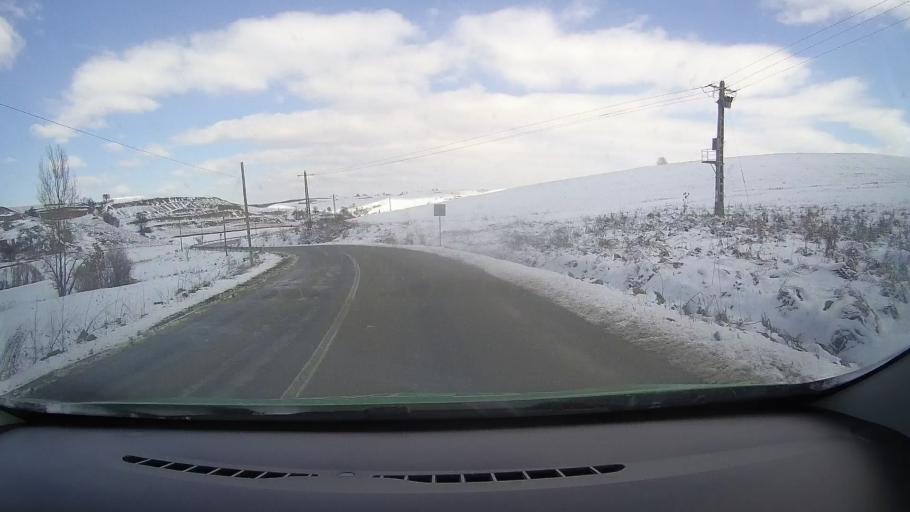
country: RO
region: Sibiu
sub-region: Comuna Barghis
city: Barghis
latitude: 45.9801
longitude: 24.5250
